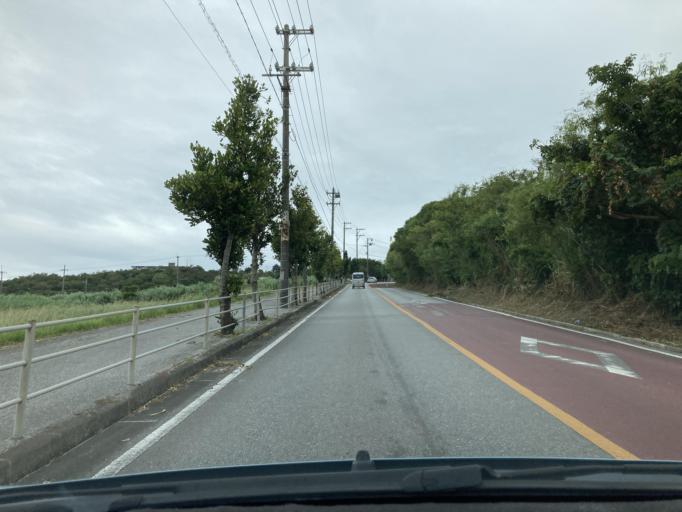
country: JP
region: Okinawa
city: Tomigusuku
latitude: 26.1662
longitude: 127.7096
